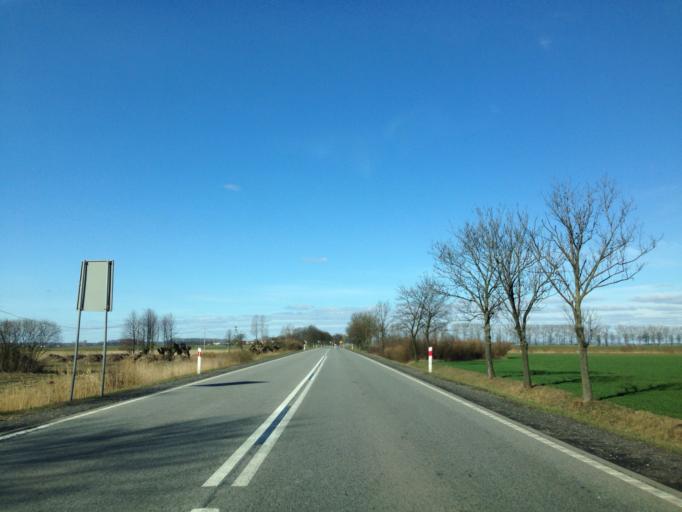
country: PL
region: Pomeranian Voivodeship
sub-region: Powiat malborski
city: Miloradz
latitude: 54.0516
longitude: 18.9299
